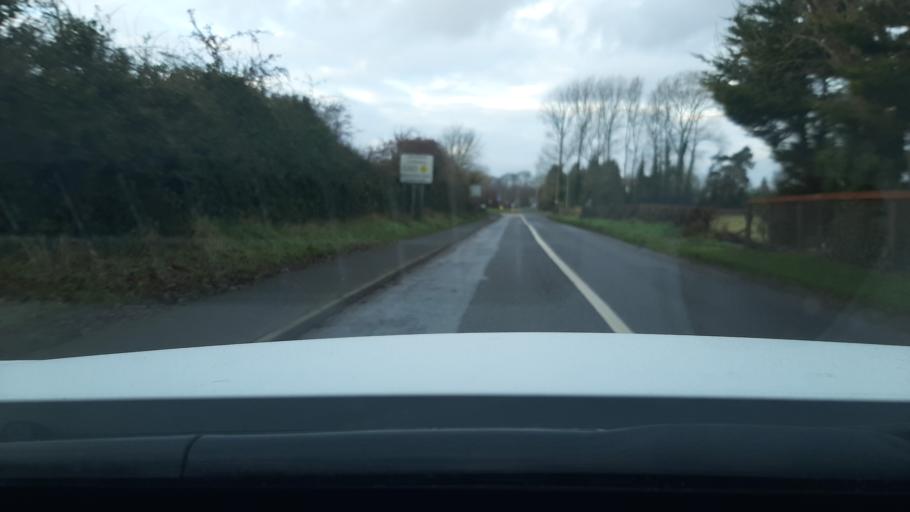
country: IE
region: Leinster
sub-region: Kildare
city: Rathangan
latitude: 53.2249
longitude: -7.0043
